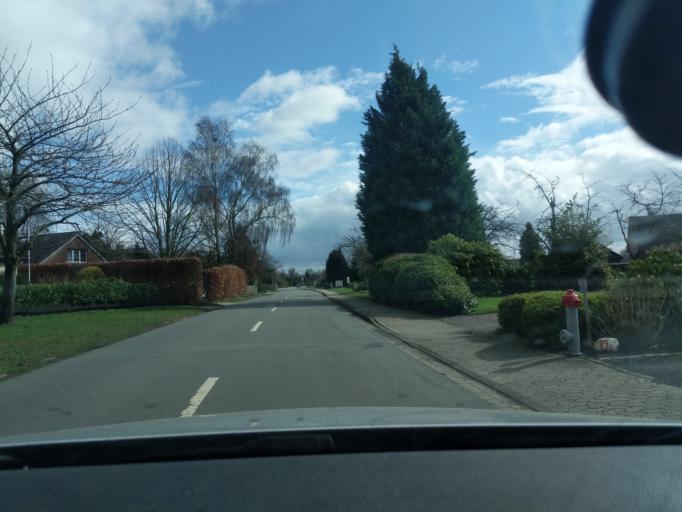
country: DE
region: Lower Saxony
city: Grunendeich
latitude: 53.5691
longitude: 9.6205
